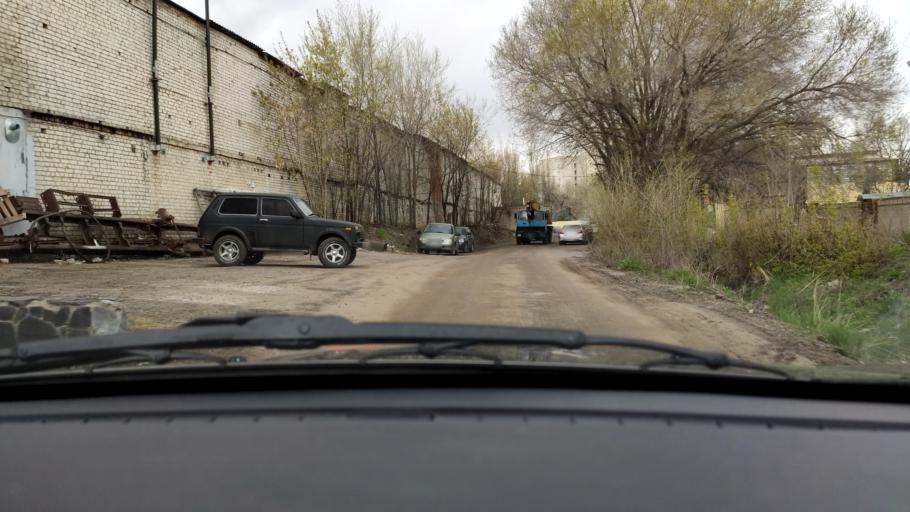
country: RU
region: Voronezj
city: Voronezh
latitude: 51.6357
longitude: 39.1570
